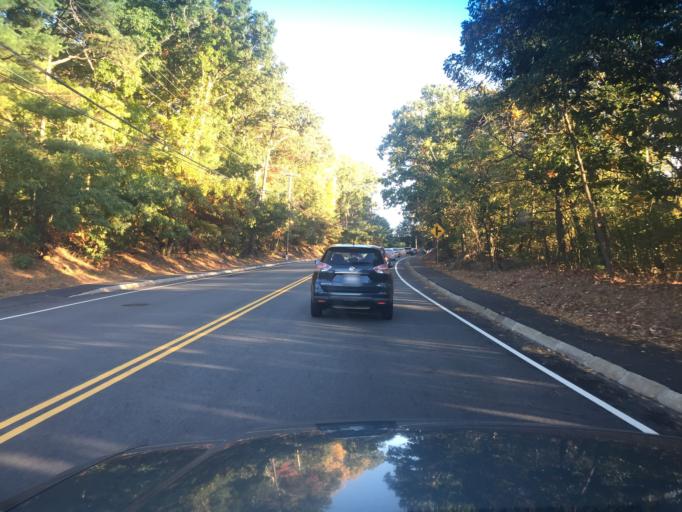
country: US
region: Massachusetts
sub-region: Middlesex County
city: Marlborough
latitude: 42.3641
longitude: -71.5548
